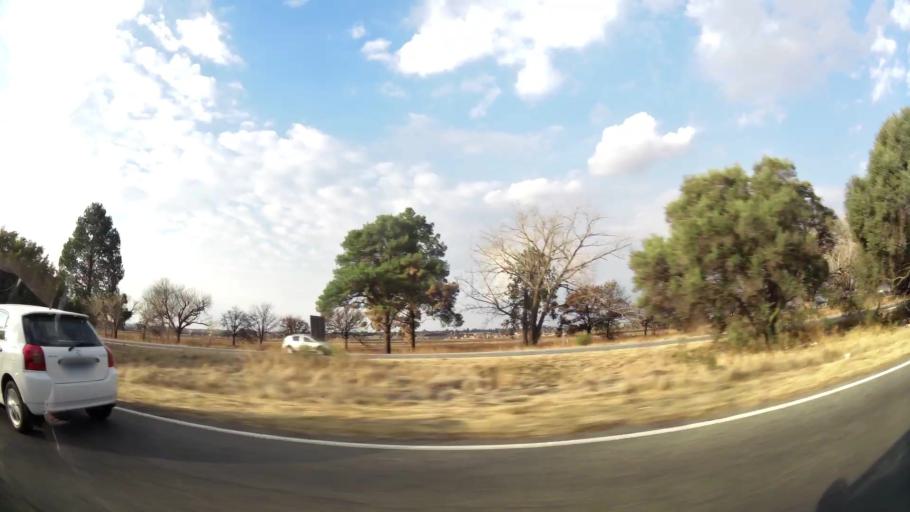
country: ZA
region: Orange Free State
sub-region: Fezile Dabi District Municipality
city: Sasolburg
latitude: -26.7922
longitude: 27.8275
